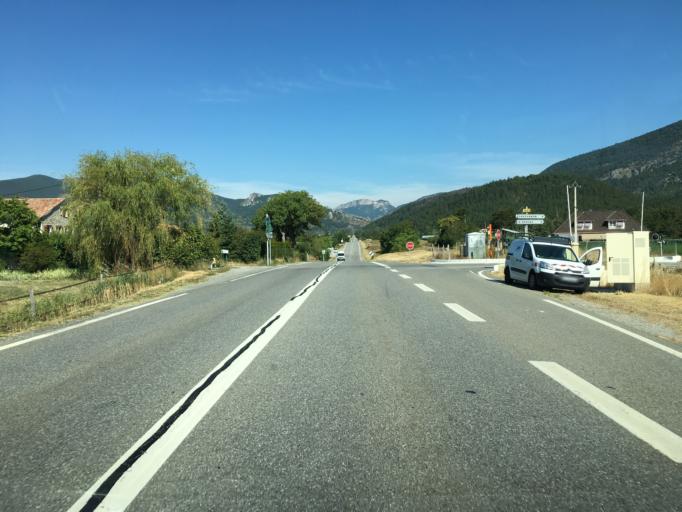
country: FR
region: Provence-Alpes-Cote d'Azur
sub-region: Departement des Hautes-Alpes
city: Serres
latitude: 44.4042
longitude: 5.7311
